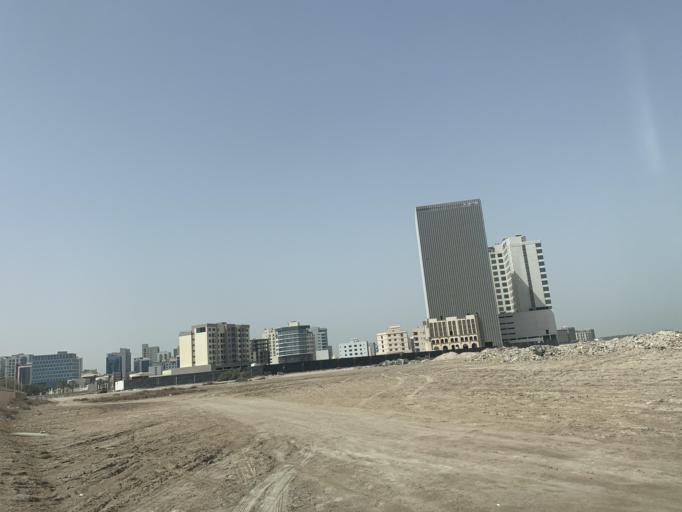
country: BH
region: Manama
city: Jidd Hafs
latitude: 26.2448
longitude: 50.5334
